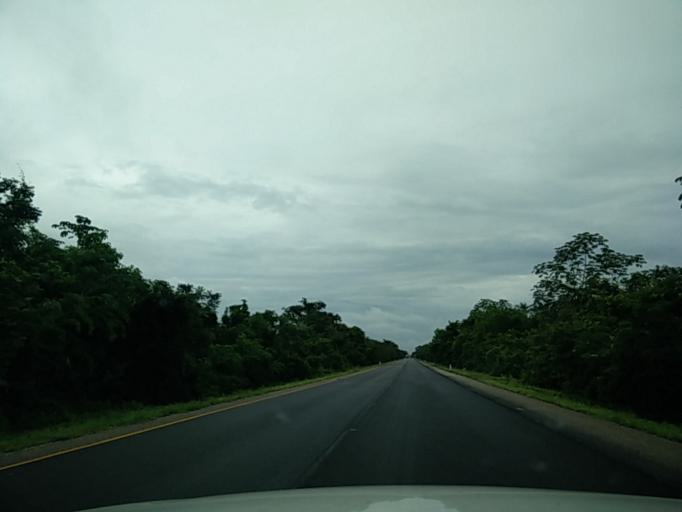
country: MX
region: Quintana Roo
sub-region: Lazaro Cardenas
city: Ignacio Zaragoza
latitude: 20.8851
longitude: -87.5637
